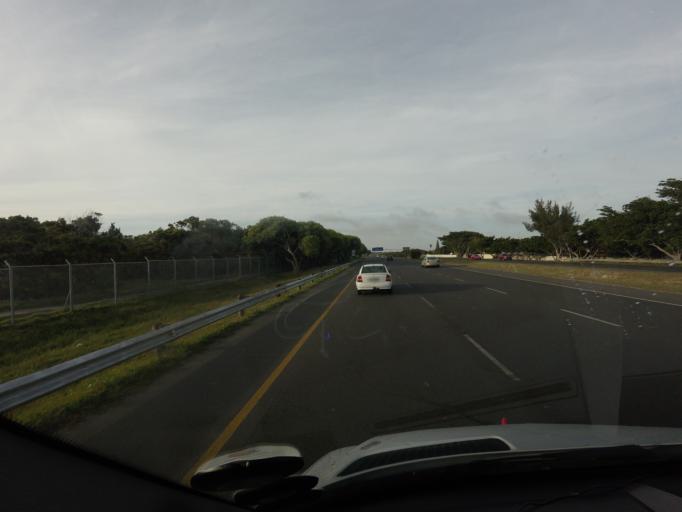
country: ZA
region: Western Cape
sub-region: City of Cape Town
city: Bergvliet
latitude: -34.0751
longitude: 18.4463
